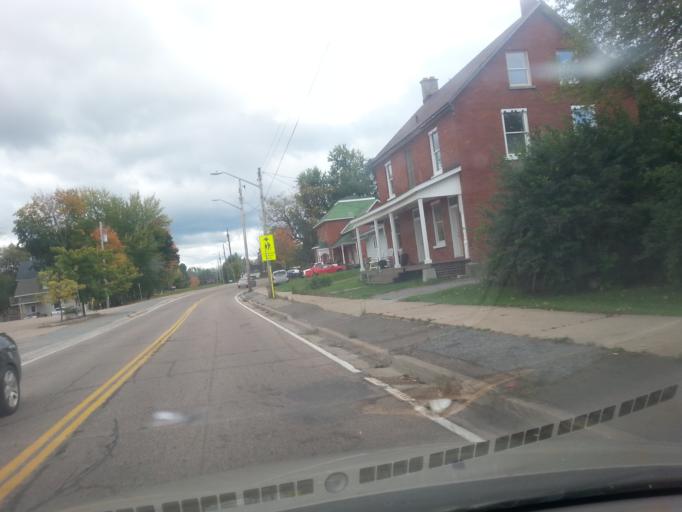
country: CA
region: Ontario
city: Pembroke
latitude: 45.5364
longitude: -77.0982
